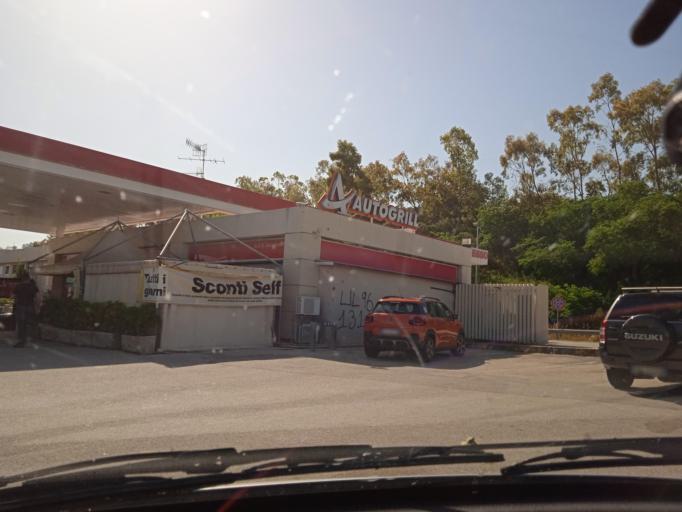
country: IT
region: Sicily
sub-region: Messina
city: Acquedolci
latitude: 38.0535
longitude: 14.6019
